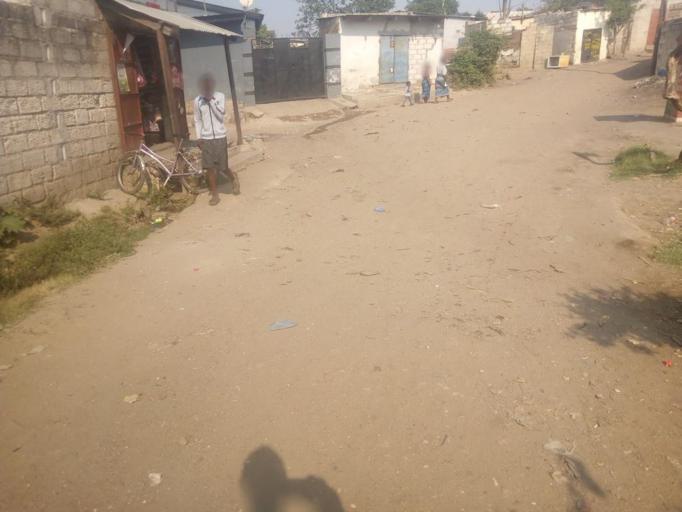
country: ZM
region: Lusaka
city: Lusaka
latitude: -15.4073
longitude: 28.3603
